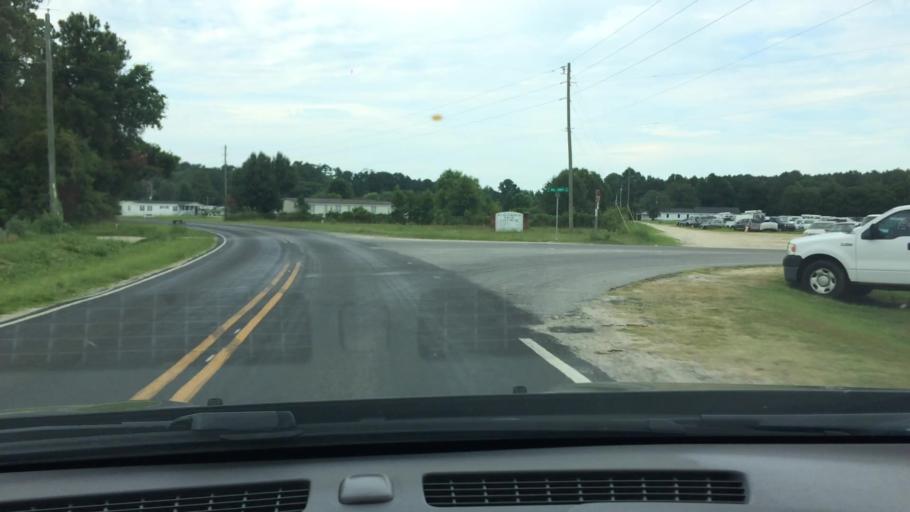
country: US
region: North Carolina
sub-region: Pitt County
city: Ayden
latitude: 35.4348
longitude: -77.4076
